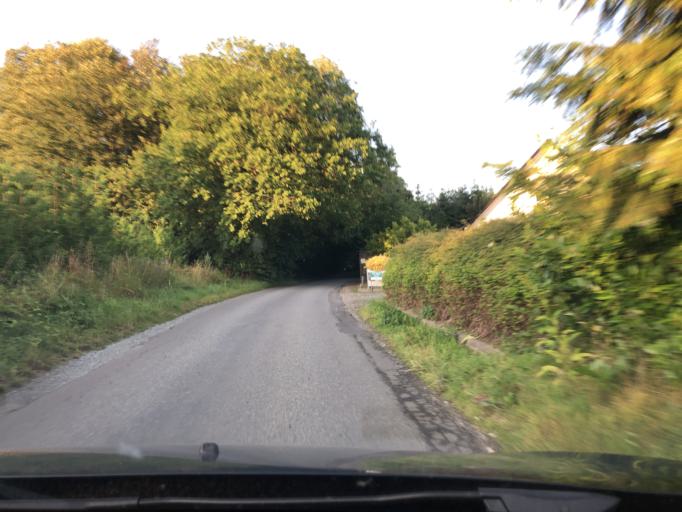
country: DK
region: South Denmark
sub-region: Vejle Kommune
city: Brejning
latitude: 55.6533
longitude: 9.7245
